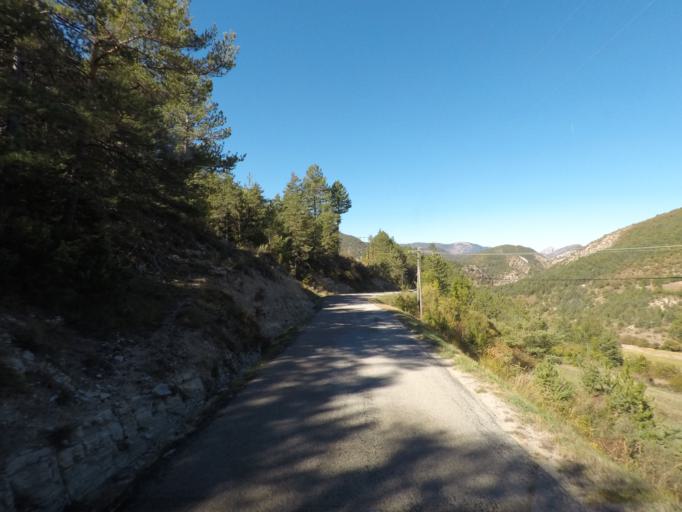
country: FR
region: Rhone-Alpes
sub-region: Departement de la Drome
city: Die
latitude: 44.5603
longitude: 5.3337
